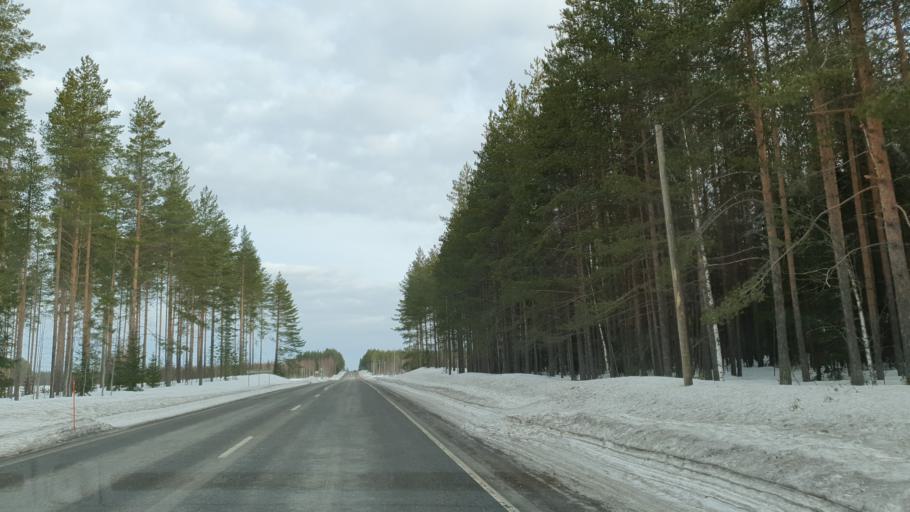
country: FI
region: Kainuu
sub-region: Kajaani
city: Vuokatti
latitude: 64.1804
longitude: 28.1920
